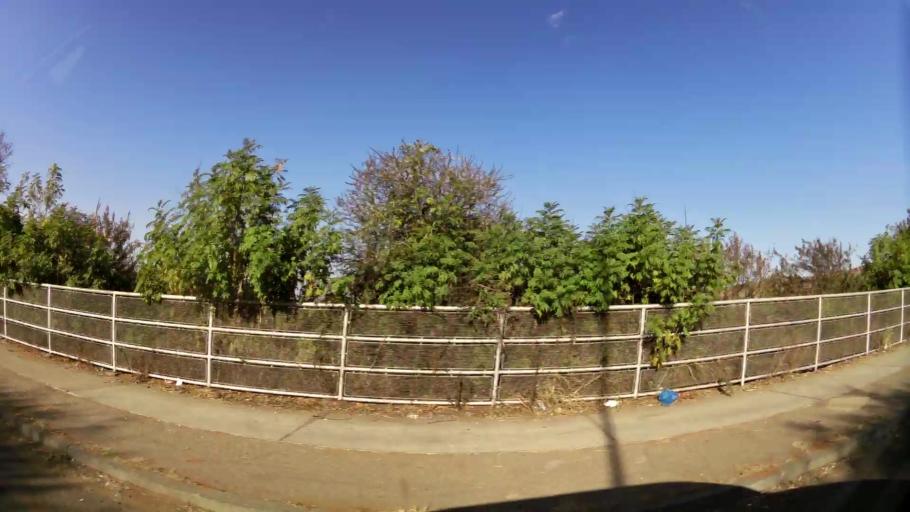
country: ZA
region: Gauteng
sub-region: City of Tshwane Metropolitan Municipality
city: Pretoria
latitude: -25.7176
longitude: 28.1542
